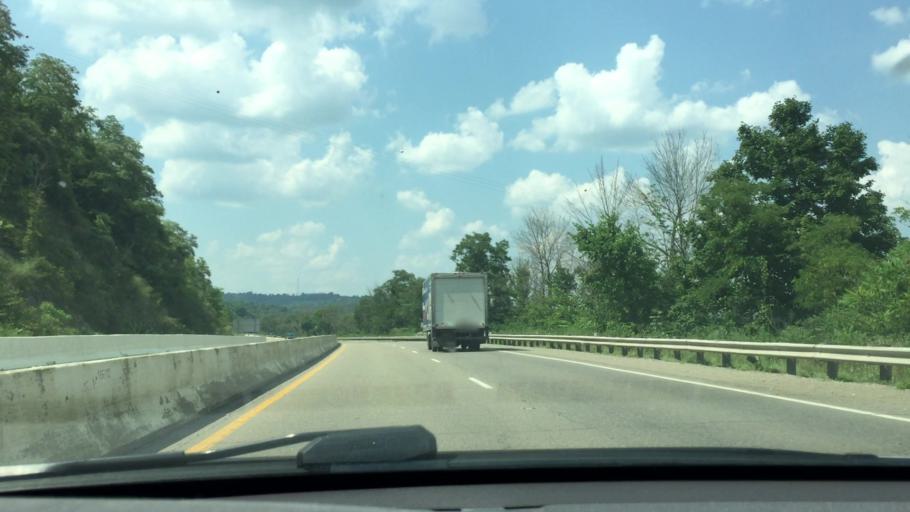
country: US
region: West Virginia
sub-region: Marshall County
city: Moundsville
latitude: 39.9201
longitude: -80.7569
